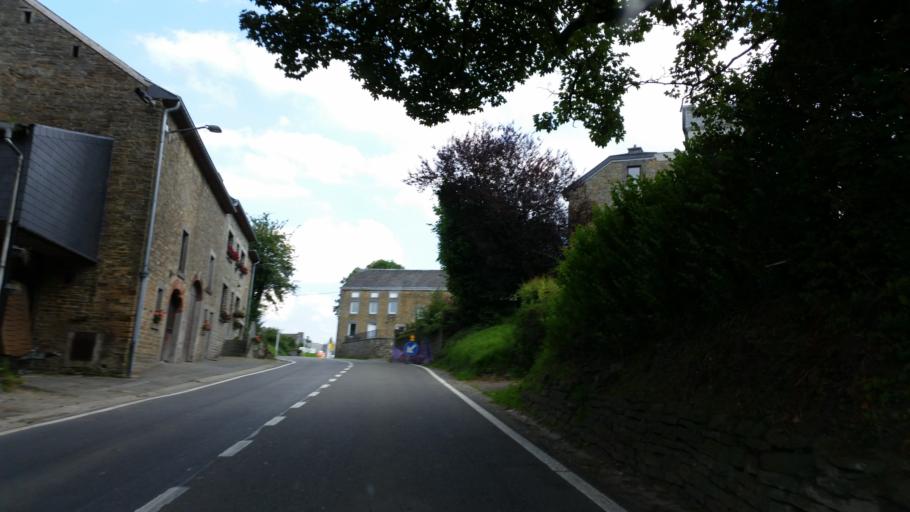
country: BE
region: Wallonia
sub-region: Province de Liege
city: Anthisnes
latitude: 50.4870
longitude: 5.5016
